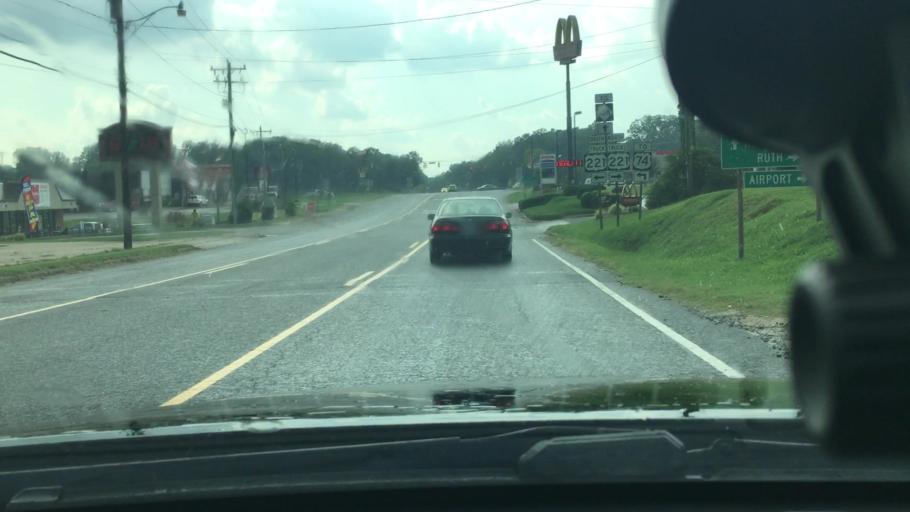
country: US
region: North Carolina
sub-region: Rutherford County
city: Spindale
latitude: 35.3621
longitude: -81.9399
